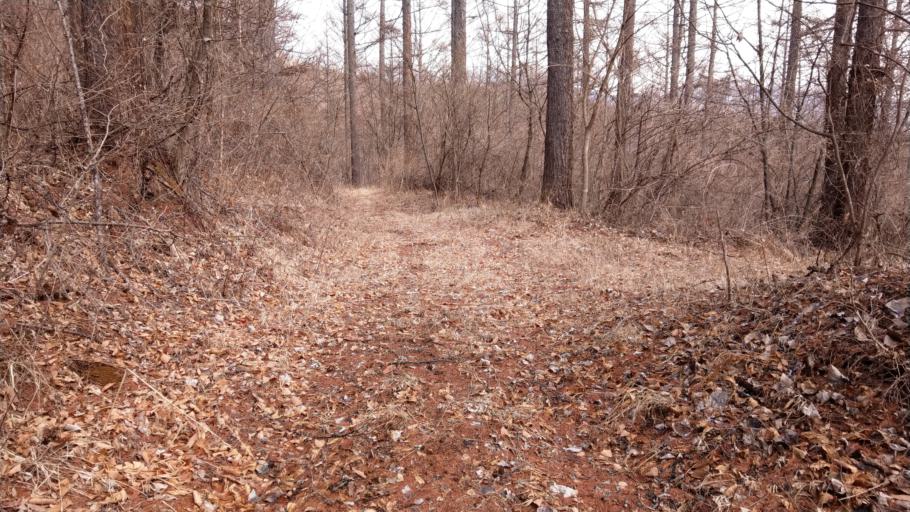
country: JP
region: Nagano
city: Komoro
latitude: 36.3752
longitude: 138.4429
